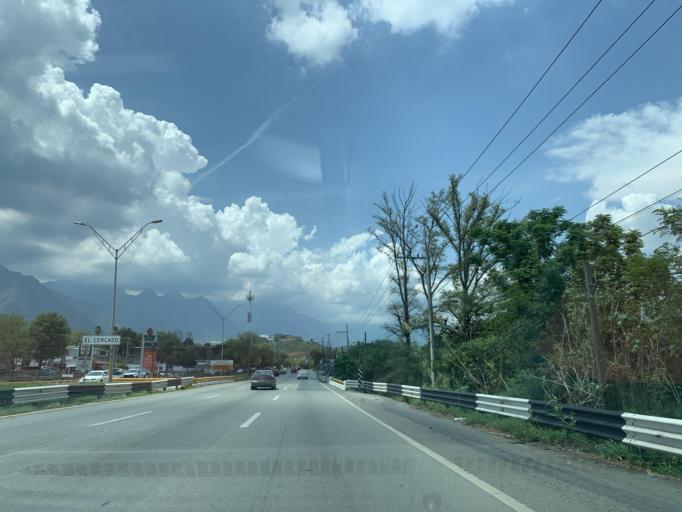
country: MX
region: Nuevo Leon
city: Santiago
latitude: 25.3972
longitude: -100.1256
